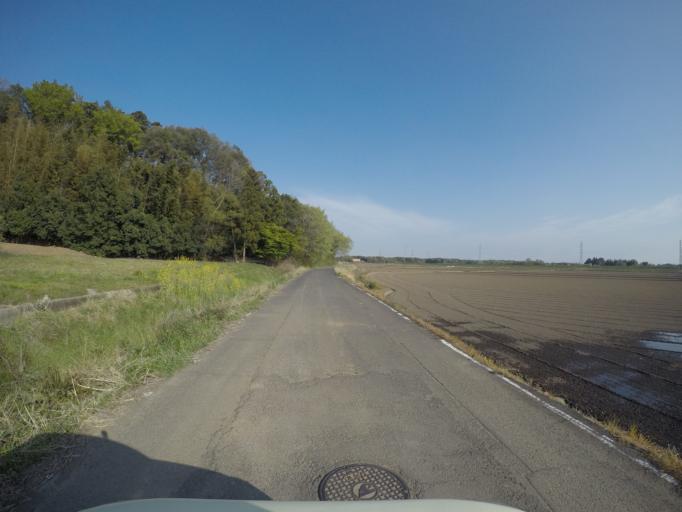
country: JP
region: Ibaraki
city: Ishige
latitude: 36.1856
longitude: 140.0087
